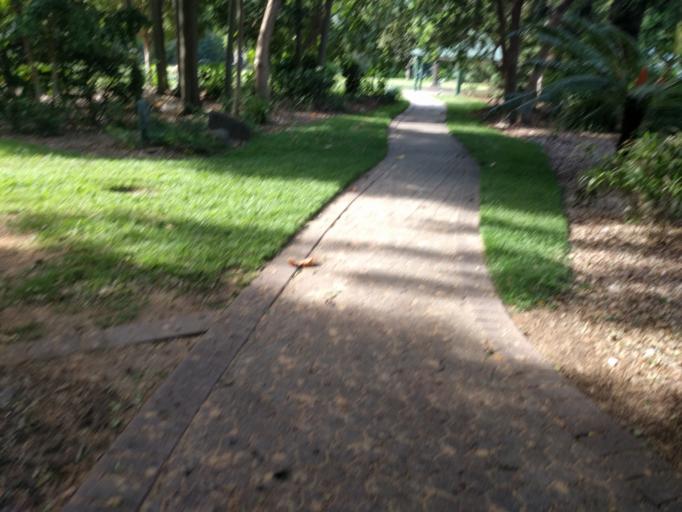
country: AU
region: Queensland
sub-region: Brisbane
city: Brisbane
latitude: -27.4736
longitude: 153.0309
